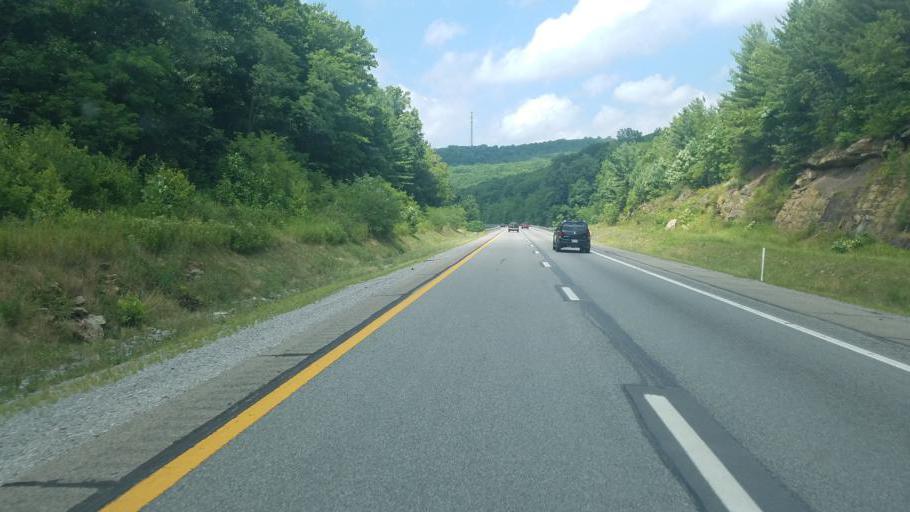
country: US
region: West Virginia
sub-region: Raleigh County
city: Shady Spring
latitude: 37.6905
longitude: -81.1290
